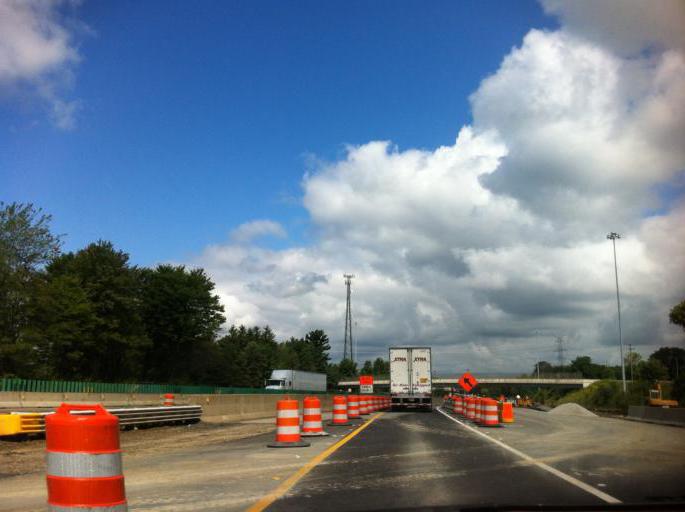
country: US
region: Ohio
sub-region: Trumbull County
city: Lordstown
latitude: 41.1163
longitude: -80.8427
